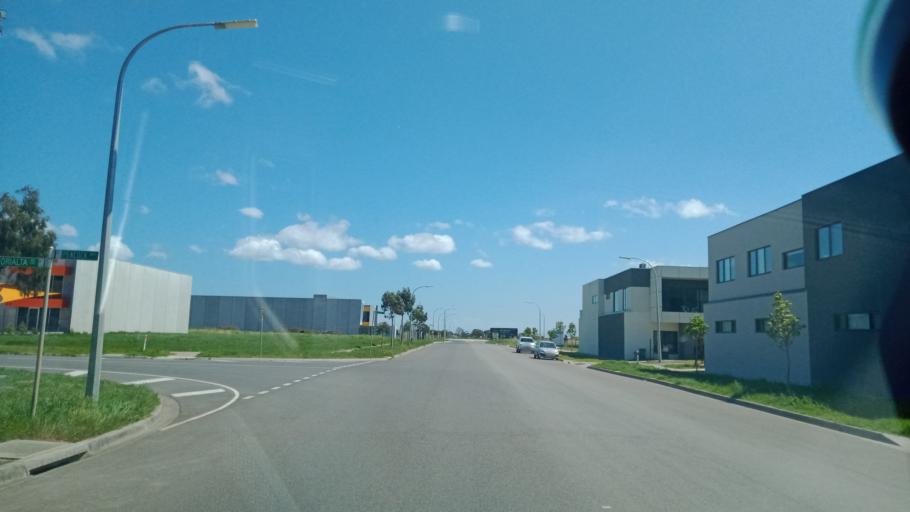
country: AU
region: Victoria
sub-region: Casey
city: Cranbourne West
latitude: -38.0914
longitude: 145.2538
